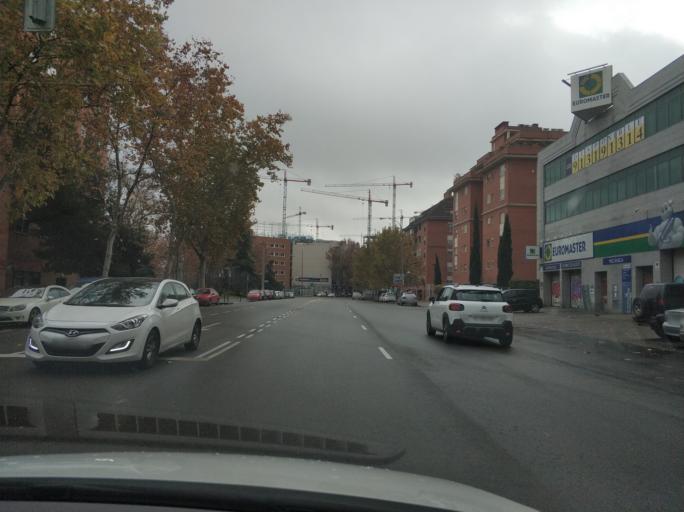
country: ES
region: Madrid
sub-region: Provincia de Madrid
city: Usera
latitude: 40.3864
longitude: -3.6974
